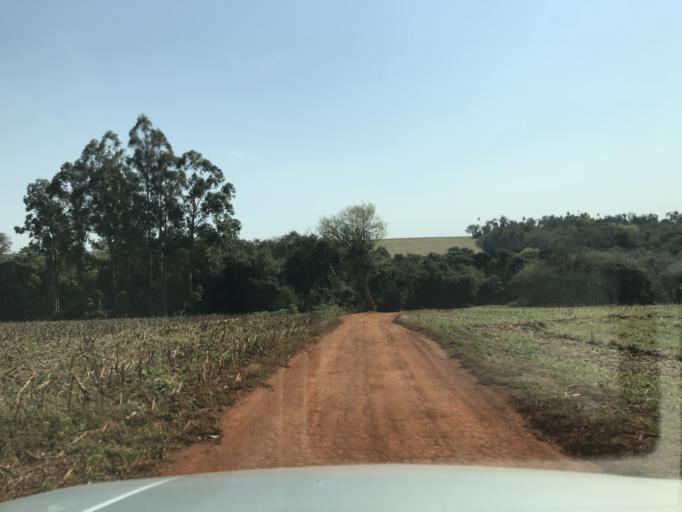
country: BR
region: Parana
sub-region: Palotina
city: Palotina
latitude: -24.2236
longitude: -53.7385
